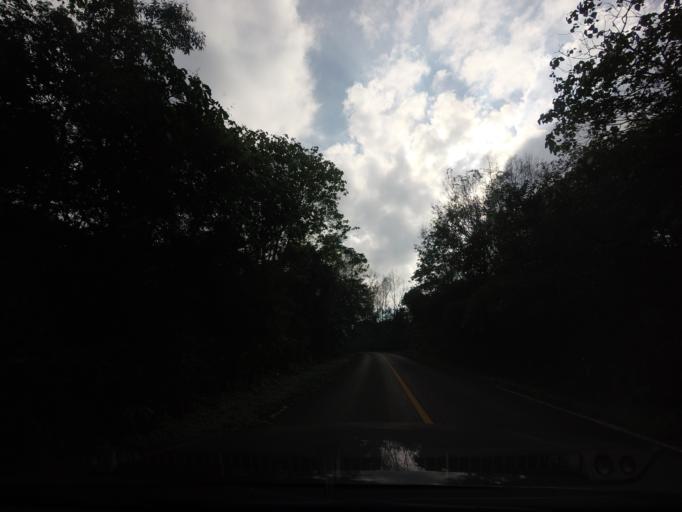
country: TH
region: Phitsanulok
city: Nakhon Thai
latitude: 16.9701
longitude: 101.0180
